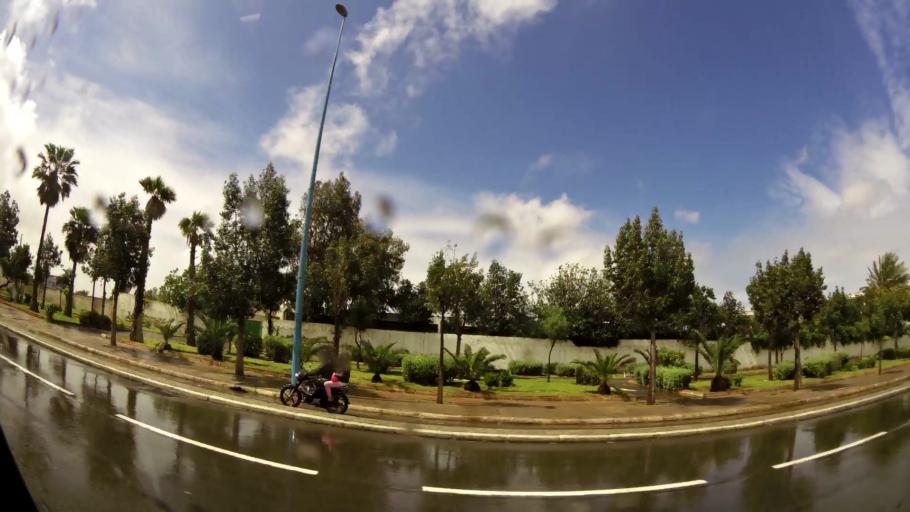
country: MA
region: Grand Casablanca
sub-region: Casablanca
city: Casablanca
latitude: 33.5520
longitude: -7.5668
